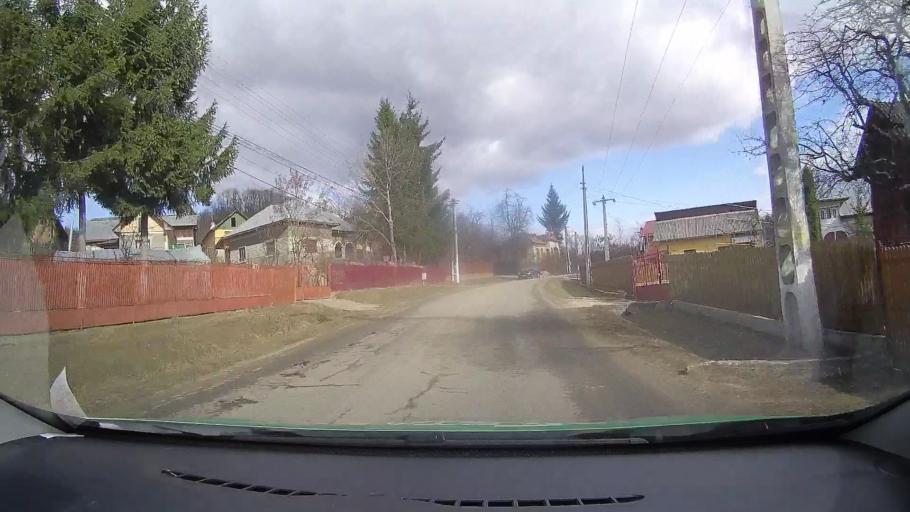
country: RO
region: Dambovita
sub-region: Comuna Buciumeni
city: Buciumeni
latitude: 45.1239
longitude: 25.4666
